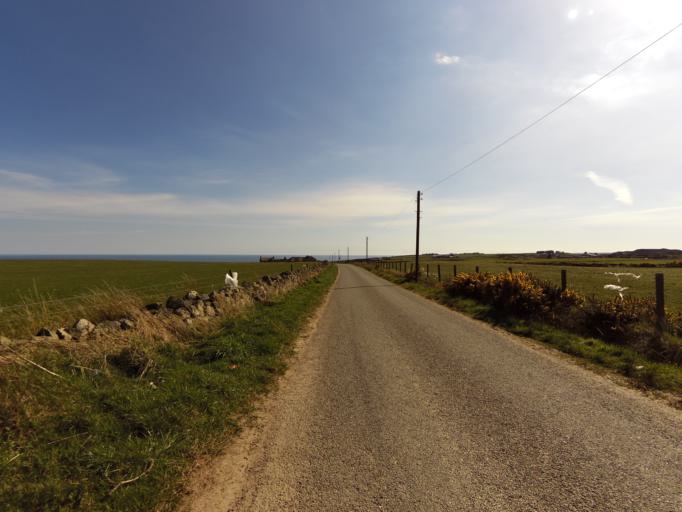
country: GB
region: Scotland
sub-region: Aberdeenshire
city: Portlethen
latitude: 57.0875
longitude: -2.0978
